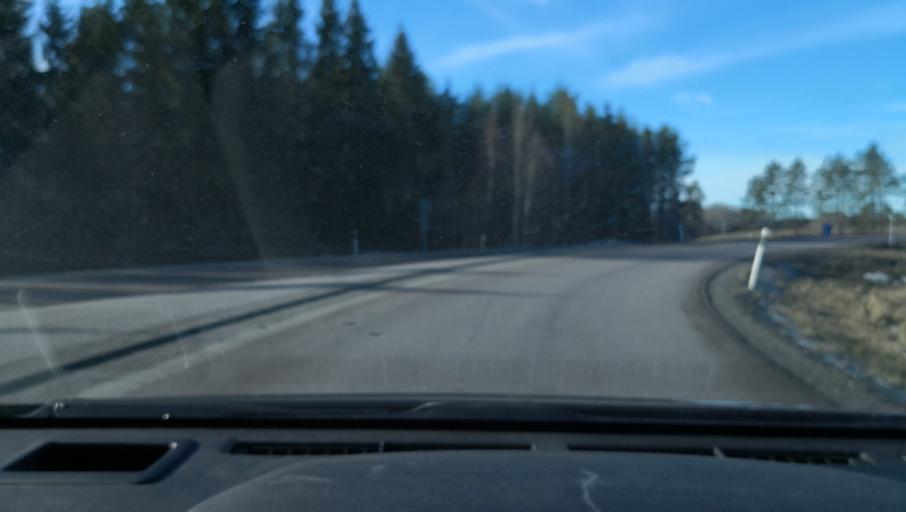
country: SE
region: Uppsala
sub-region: Enkopings Kommun
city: Enkoping
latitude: 59.6460
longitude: 17.1454
